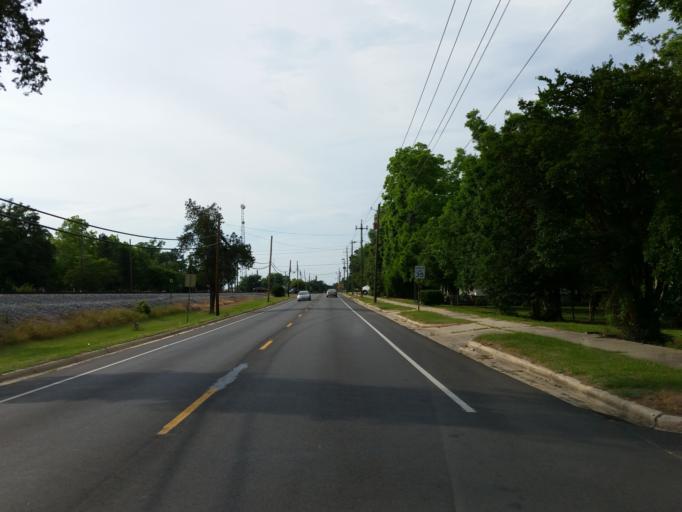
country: US
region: Georgia
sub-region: Turner County
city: Ashburn
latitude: 31.6997
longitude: -83.6504
